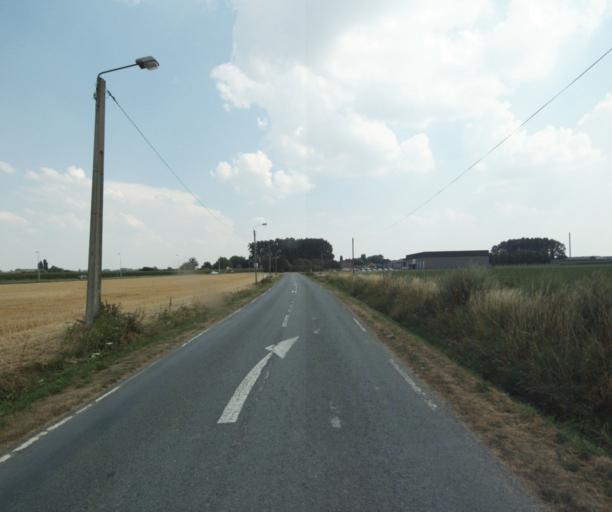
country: FR
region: Nord-Pas-de-Calais
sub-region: Departement du Nord
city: Comines
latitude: 50.7357
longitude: 3.0167
